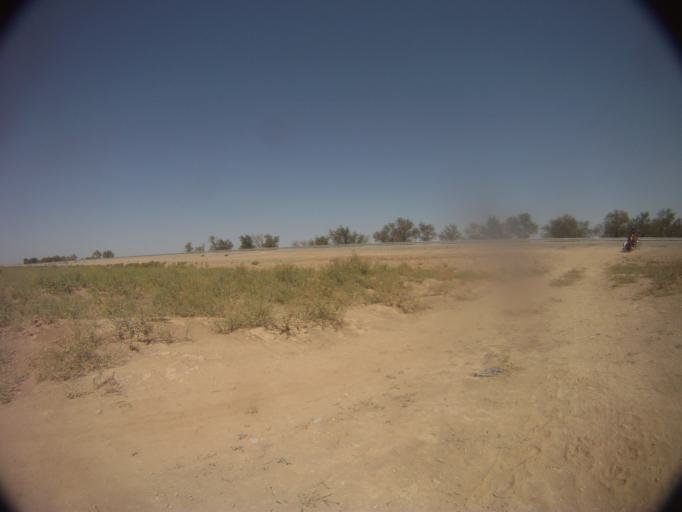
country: KZ
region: Ongtustik Qazaqstan
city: Bayaldyr
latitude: 43.0569
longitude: 68.6891
